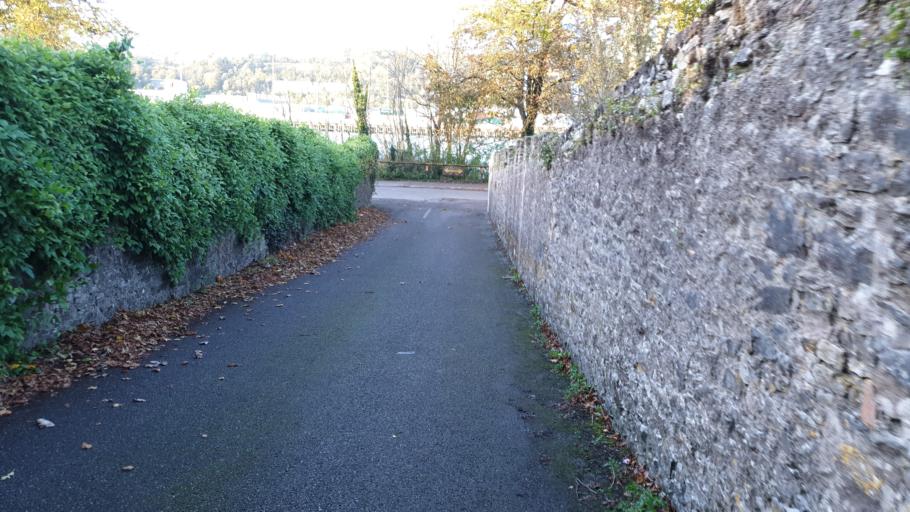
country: IE
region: Munster
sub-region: County Cork
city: Cork
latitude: 51.8980
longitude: -8.4169
